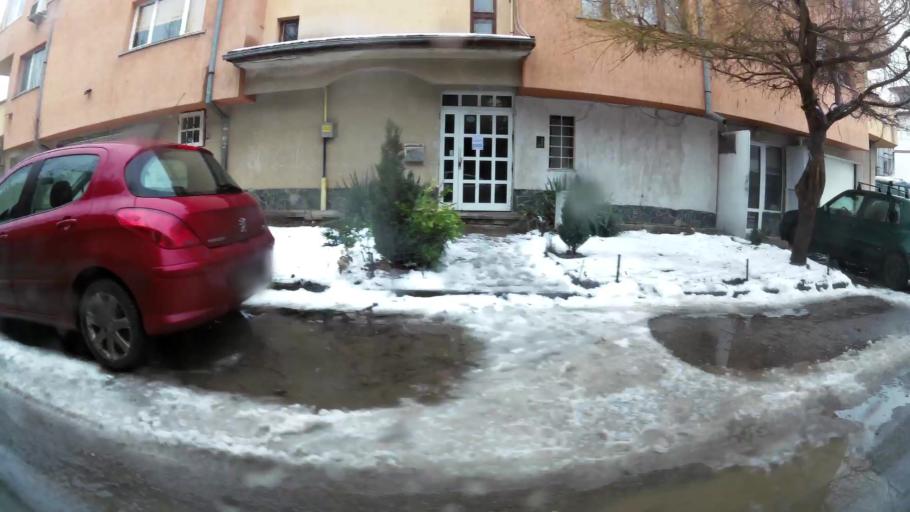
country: BG
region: Sofia-Capital
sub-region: Stolichna Obshtina
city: Sofia
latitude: 42.6587
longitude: 23.2767
